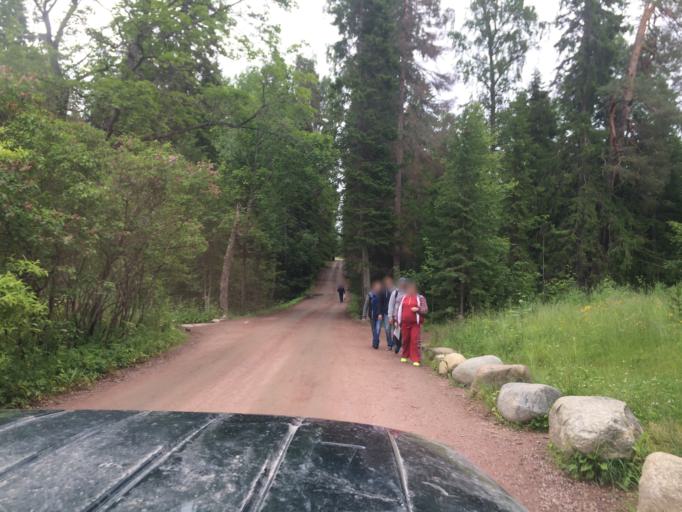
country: RU
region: Republic of Karelia
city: Sortavala
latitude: 61.3699
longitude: 30.9023
